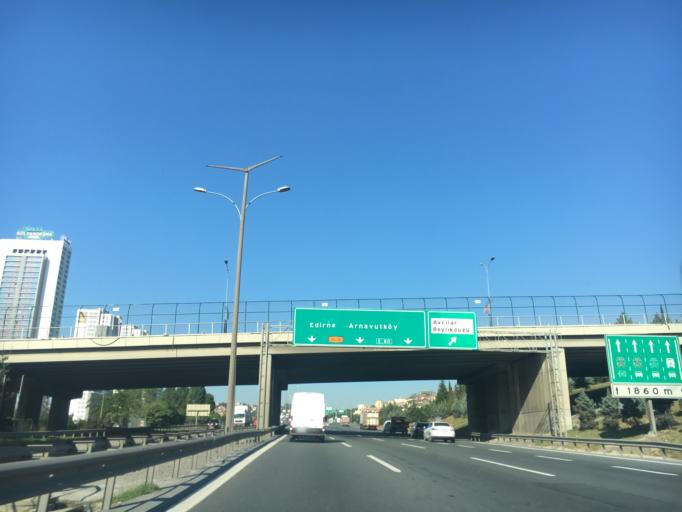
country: TR
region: Istanbul
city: Esenyurt
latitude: 41.0581
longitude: 28.6923
